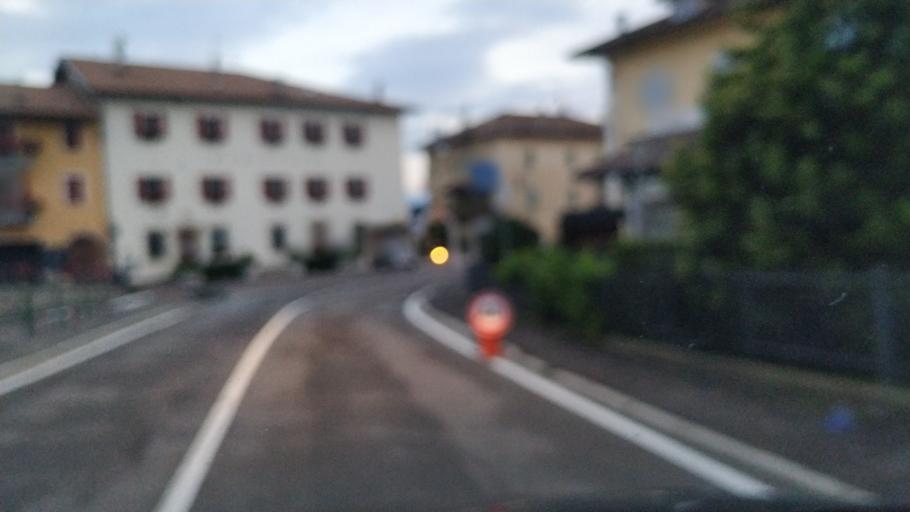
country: IT
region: Trentino-Alto Adige
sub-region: Provincia di Trento
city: Brez
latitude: 46.4314
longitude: 11.1076
